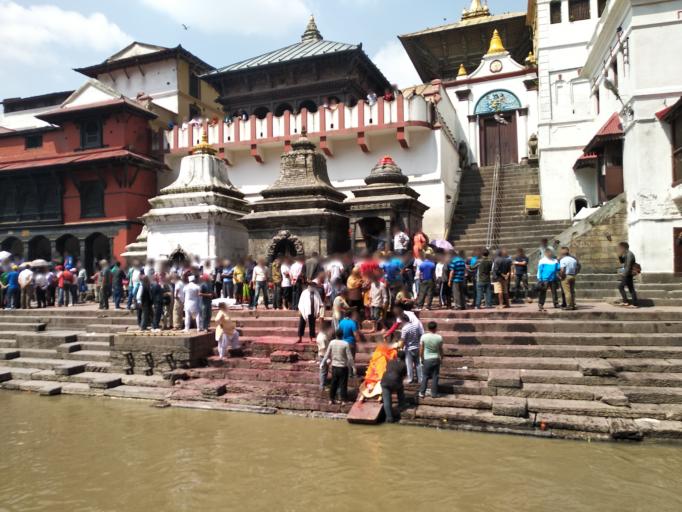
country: NP
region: Central Region
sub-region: Bagmati Zone
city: Kathmandu
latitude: 27.7103
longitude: 85.3491
